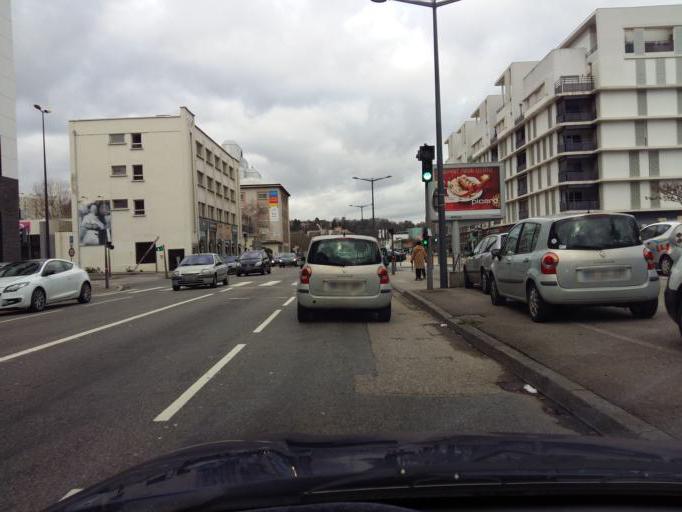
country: FR
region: Rhone-Alpes
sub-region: Departement du Rhone
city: Ecully
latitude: 45.7829
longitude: 4.8075
